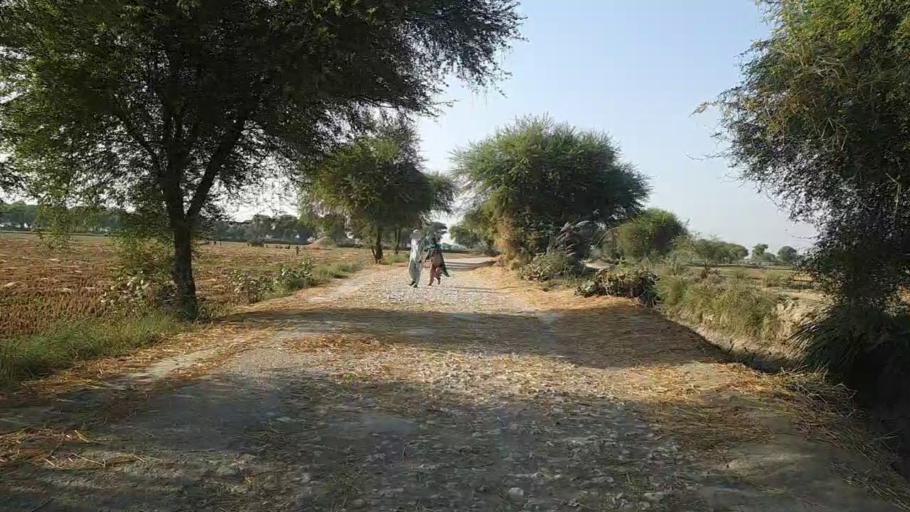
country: PK
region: Sindh
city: Kashmor
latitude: 28.4054
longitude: 69.4148
